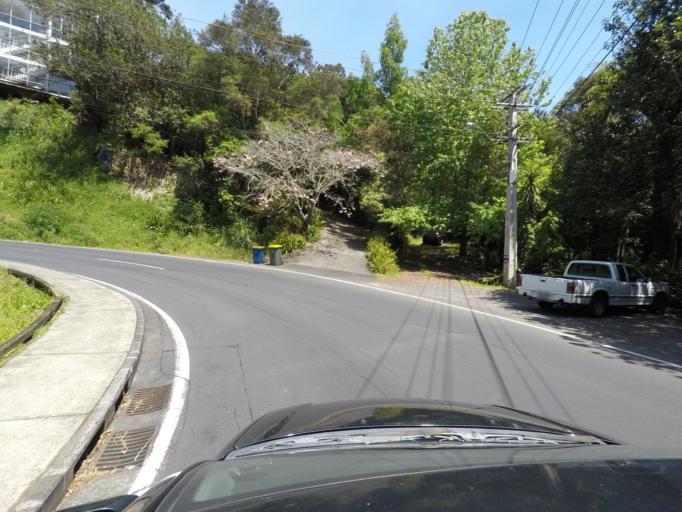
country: NZ
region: Auckland
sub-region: Auckland
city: Titirangi
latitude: -36.9612
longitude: 174.6397
